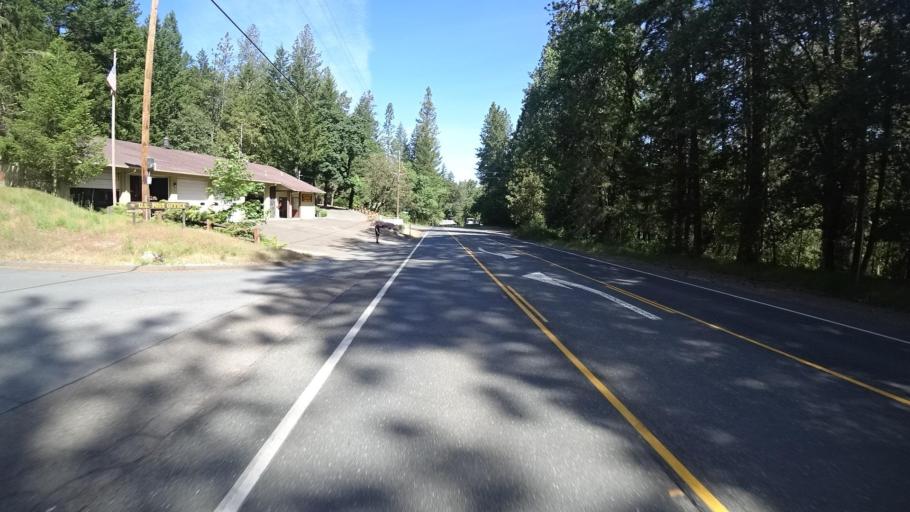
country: US
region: California
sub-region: Lake County
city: Cobb
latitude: 38.8220
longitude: -122.7203
